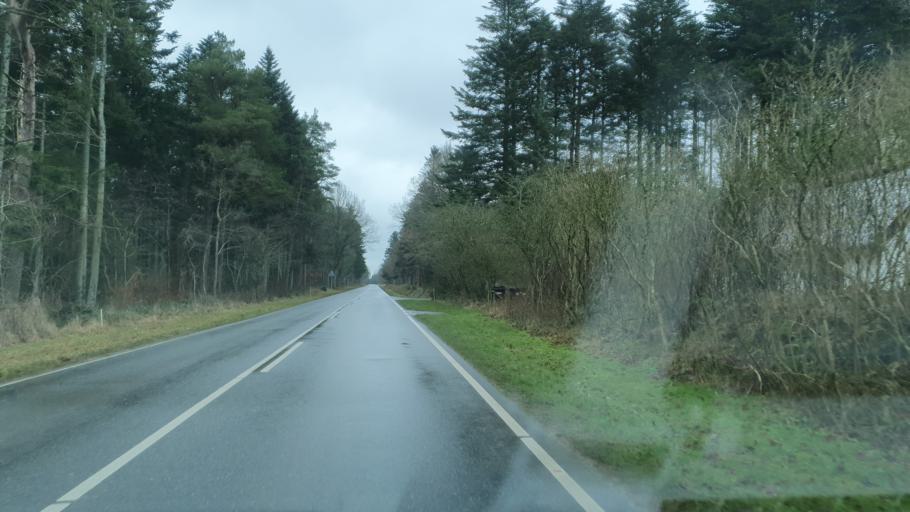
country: DK
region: North Denmark
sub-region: Jammerbugt Kommune
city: Fjerritslev
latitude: 57.1202
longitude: 9.1262
